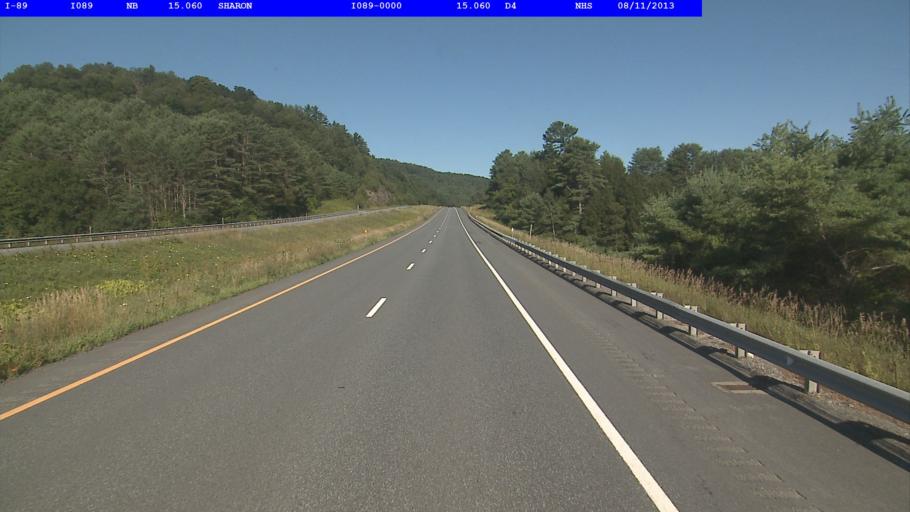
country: US
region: Vermont
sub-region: Windsor County
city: Woodstock
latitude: 43.7832
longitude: -72.4839
